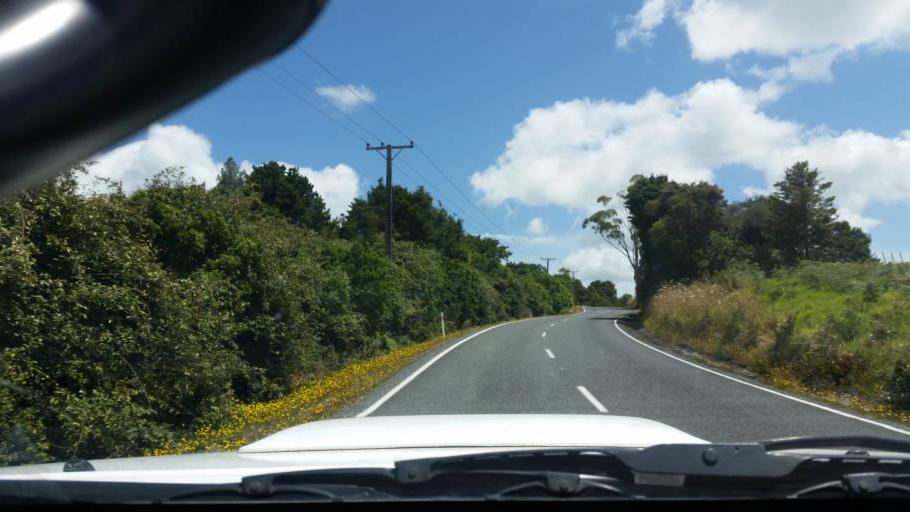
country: NZ
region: Northland
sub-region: Whangarei
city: Ruakaka
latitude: -36.0635
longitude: 174.2699
